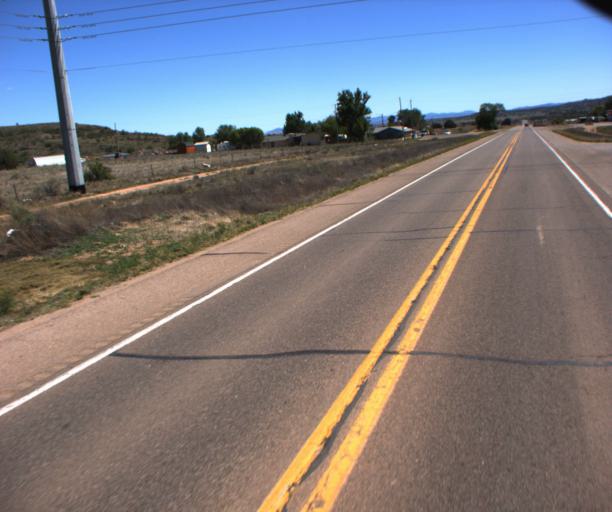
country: US
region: Arizona
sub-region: Yavapai County
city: Paulden
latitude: 34.8880
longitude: -112.4677
